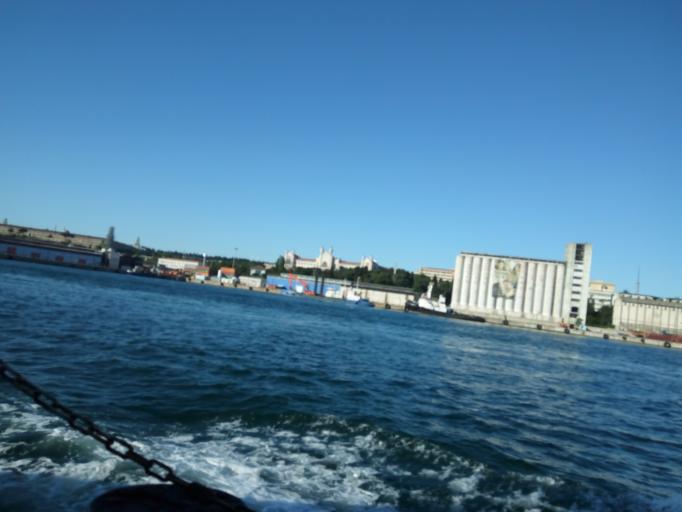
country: TR
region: Istanbul
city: UEskuedar
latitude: 40.9977
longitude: 29.0143
